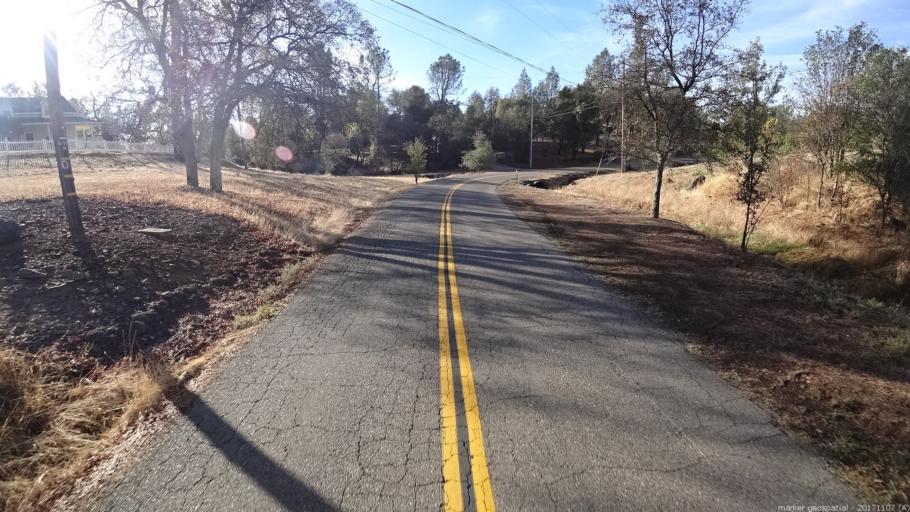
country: US
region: California
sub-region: Shasta County
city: Shasta
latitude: 40.5414
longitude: -122.4555
